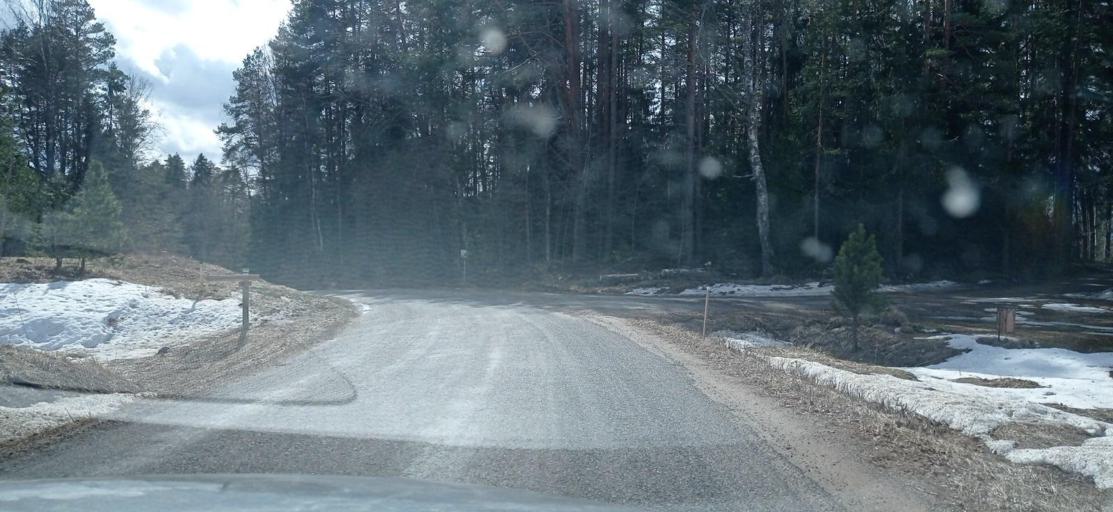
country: EE
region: Polvamaa
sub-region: Polva linn
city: Polva
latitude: 58.1409
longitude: 27.0210
